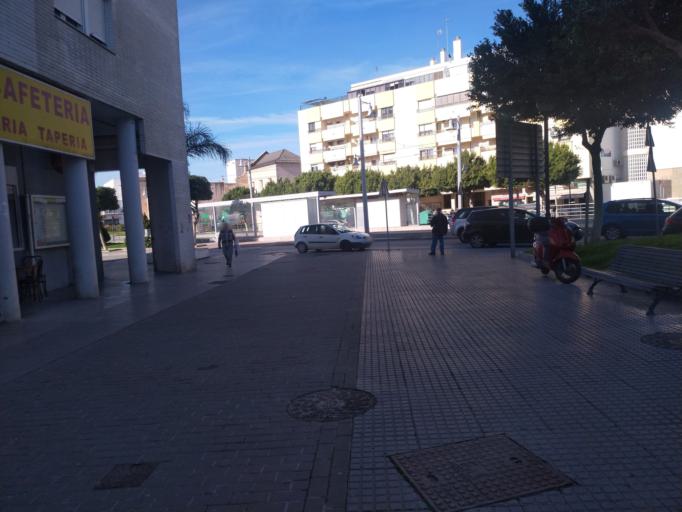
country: ES
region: Andalusia
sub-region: Provincia de Cadiz
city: San Fernando
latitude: 36.4676
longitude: -6.1906
